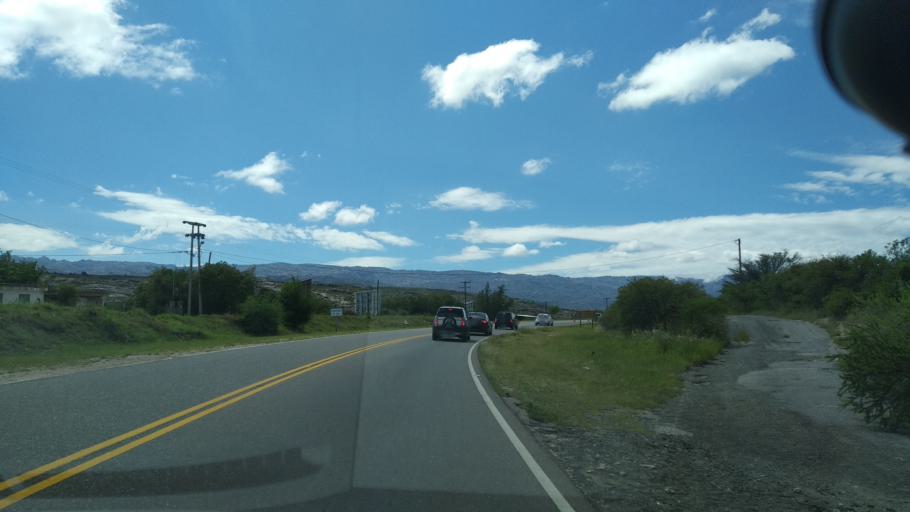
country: AR
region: Cordoba
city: Mina Clavero
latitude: -31.7491
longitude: -64.9796
